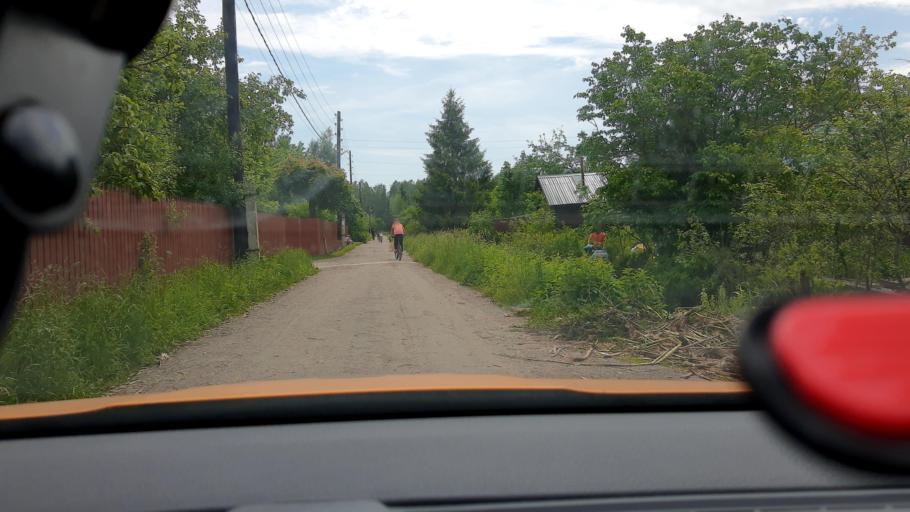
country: RU
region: Moskovskaya
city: Chupryakovo
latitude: 55.5644
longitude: 36.6596
